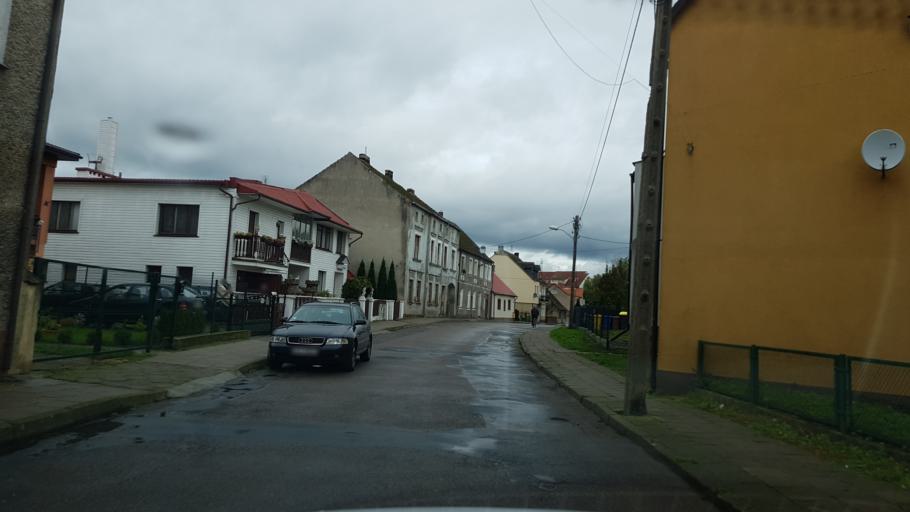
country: PL
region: West Pomeranian Voivodeship
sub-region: Powiat kamienski
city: Wolin
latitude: 53.8394
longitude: 14.6149
